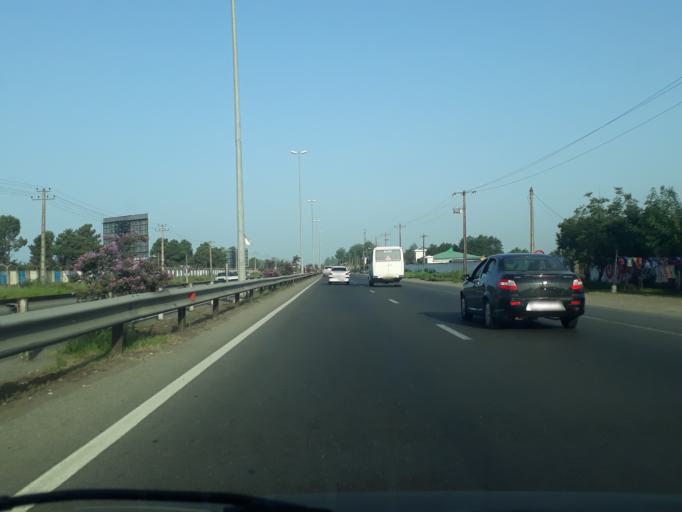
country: IR
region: Gilan
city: Bandar-e Anzali
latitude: 37.4588
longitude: 49.5992
